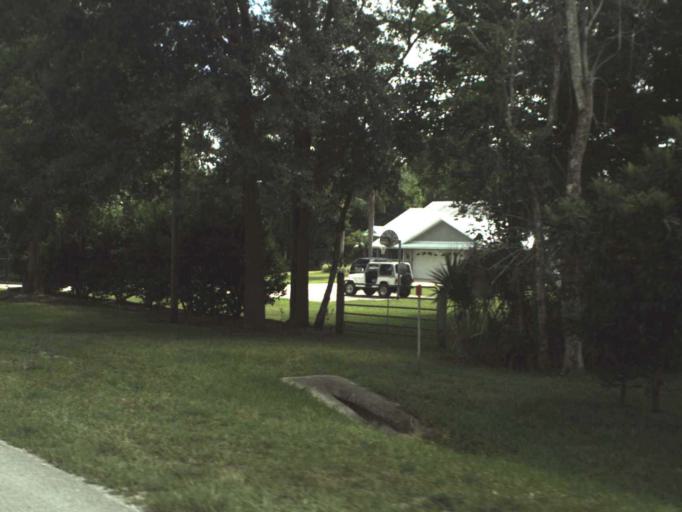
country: US
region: Florida
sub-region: Volusia County
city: Samsula-Spruce Creek
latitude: 29.0015
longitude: -81.0704
